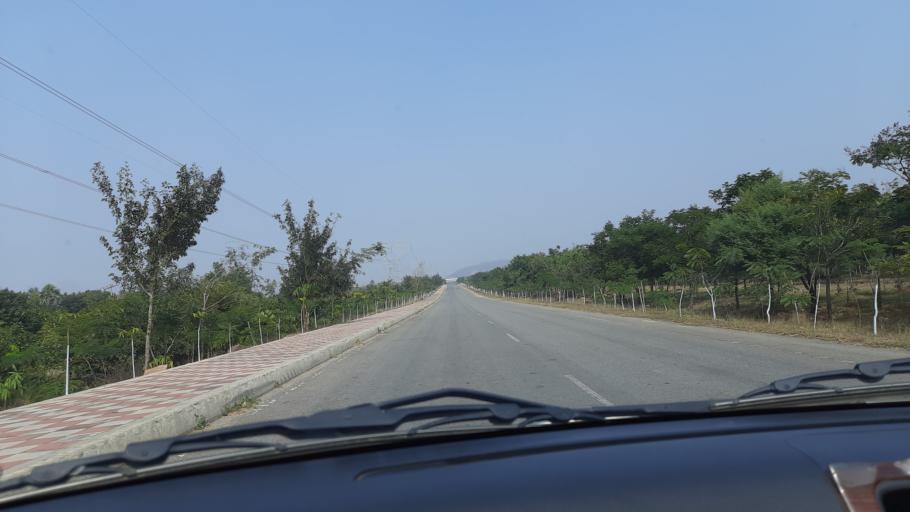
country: IN
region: Telangana
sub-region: Rangareddi
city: Lal Bahadur Nagar
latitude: 17.3003
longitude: 78.6535
